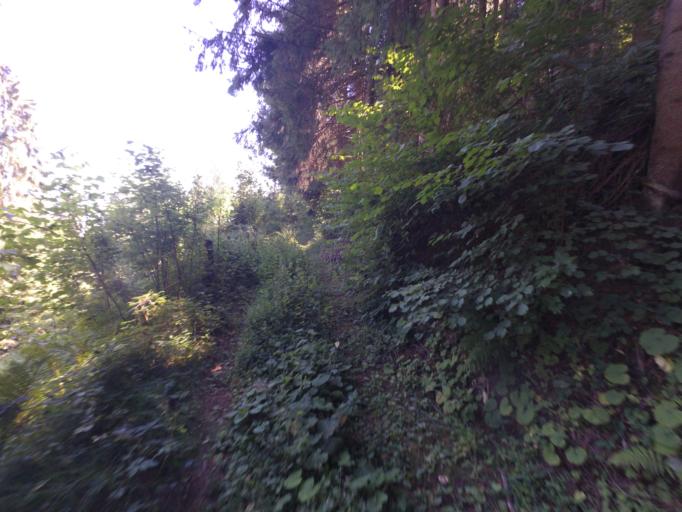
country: AT
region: Salzburg
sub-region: Politischer Bezirk Sankt Johann im Pongau
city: Goldegg
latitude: 47.3291
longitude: 13.1215
